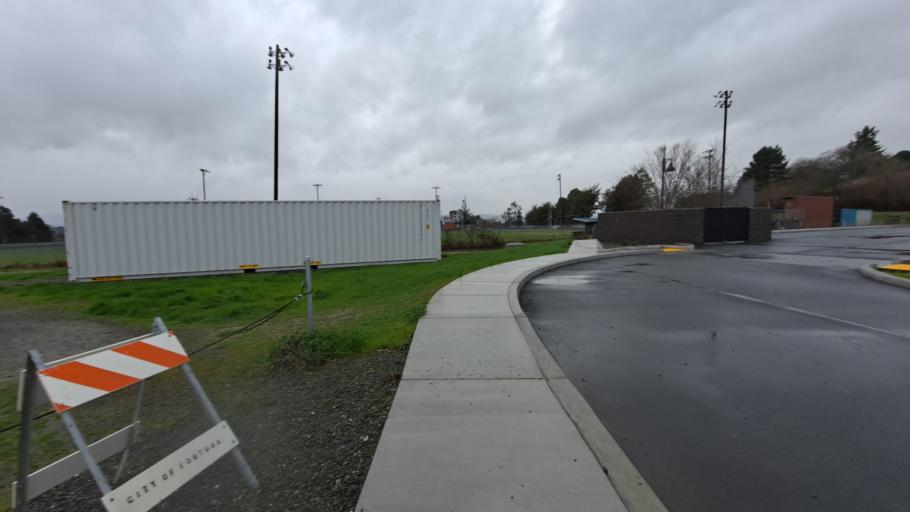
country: US
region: California
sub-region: Humboldt County
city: Fortuna
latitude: 40.5935
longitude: -124.1348
